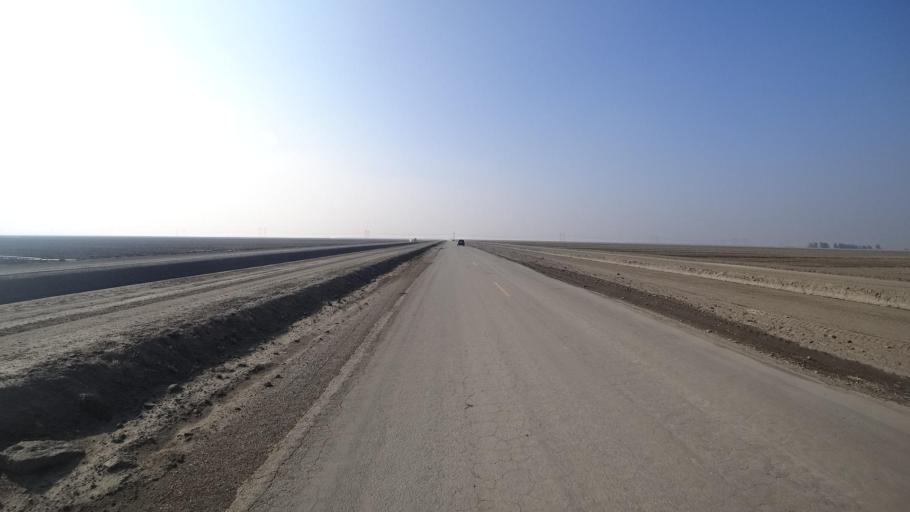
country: US
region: California
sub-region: Kern County
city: Greenfield
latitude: 35.1514
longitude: -119.0317
